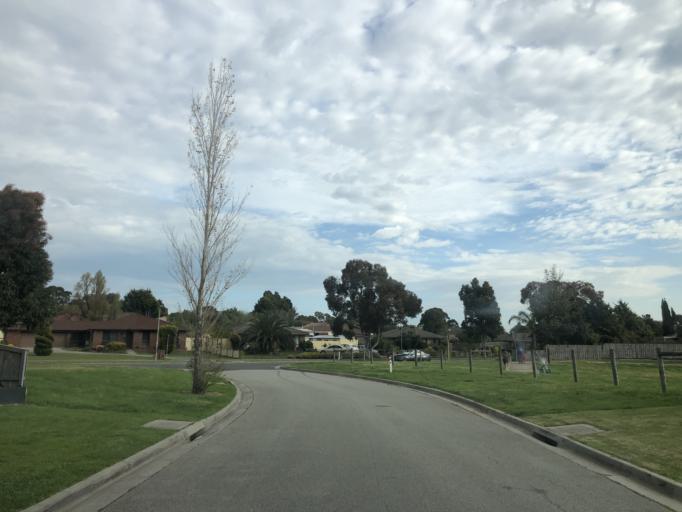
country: AU
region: Victoria
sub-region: Casey
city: Hampton Park
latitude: -38.0217
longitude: 145.2530
